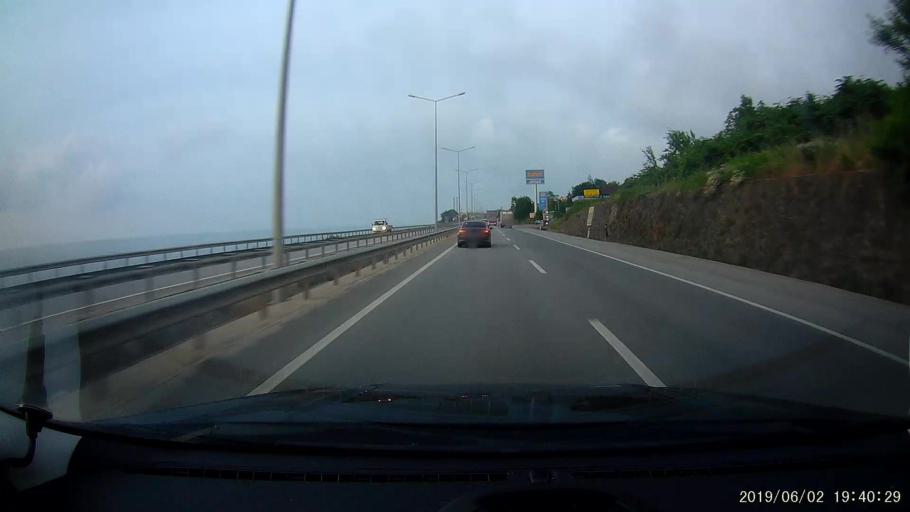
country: TR
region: Giresun
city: Kesap
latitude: 40.9151
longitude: 38.4608
